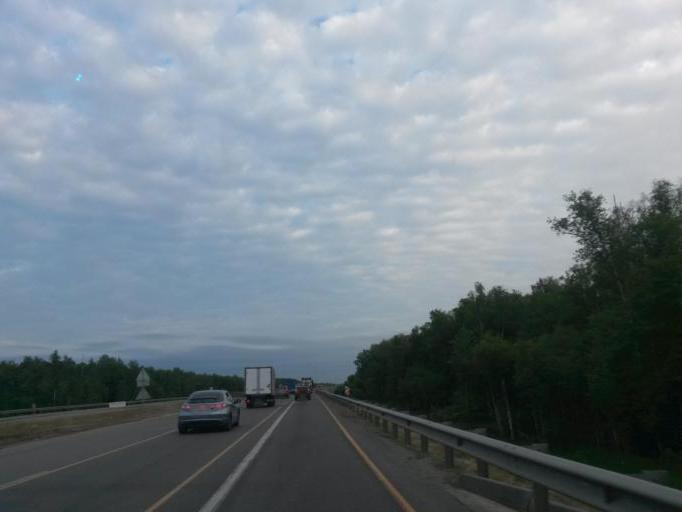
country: RU
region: Moskovskaya
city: Lyubuchany
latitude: 55.2148
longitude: 37.5341
